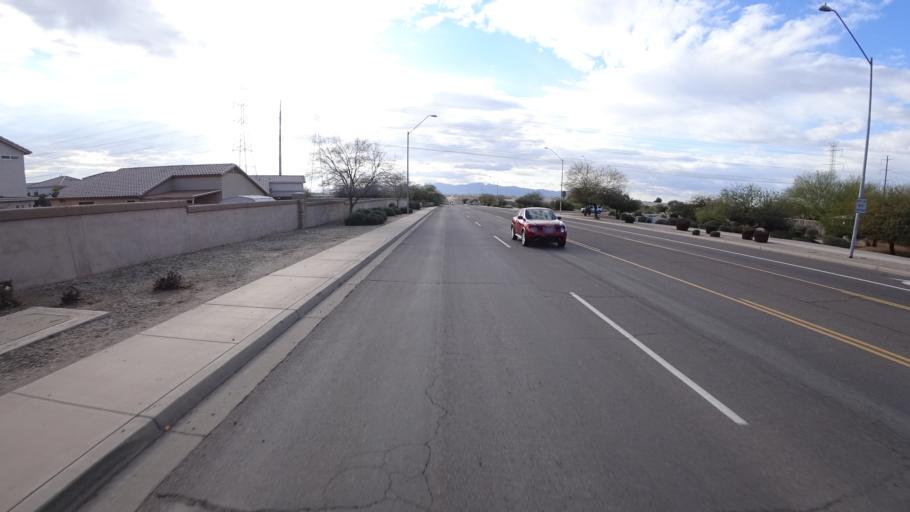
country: US
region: Arizona
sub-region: Maricopa County
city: Youngtown
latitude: 33.5509
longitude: -112.2971
